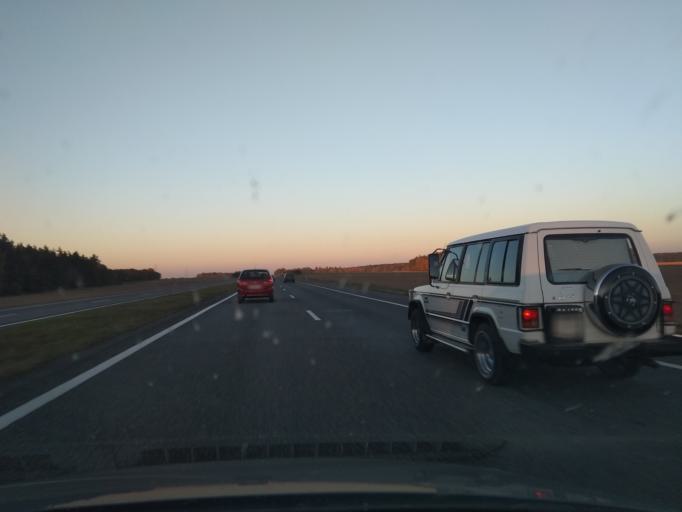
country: BY
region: Minsk
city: Haradzyeya
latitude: 53.3673
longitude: 26.4867
